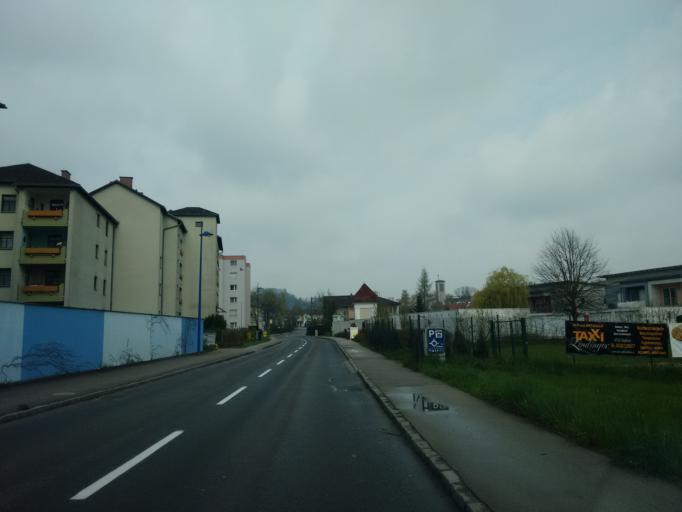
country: AT
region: Upper Austria
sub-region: Politischer Bezirk Grieskirchen
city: Bad Schallerbach
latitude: 48.2250
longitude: 13.9284
